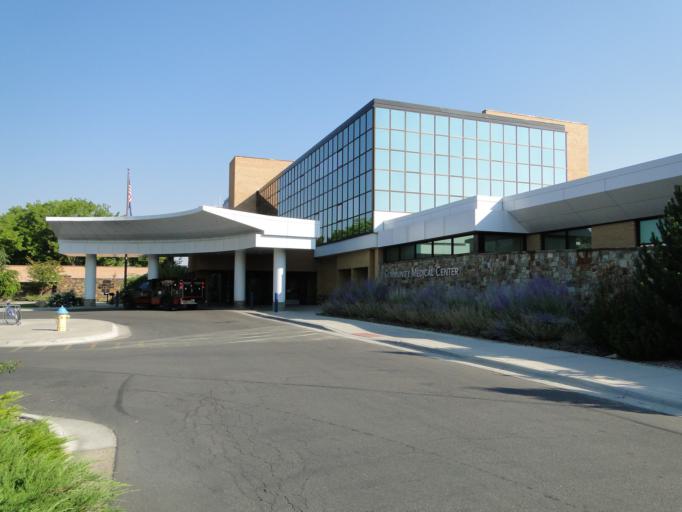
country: US
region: Montana
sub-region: Missoula County
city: Orchard Homes
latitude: 46.8469
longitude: -114.0474
